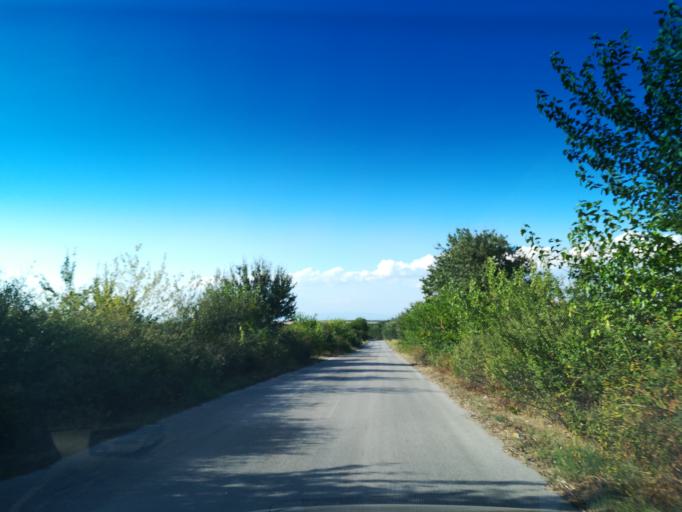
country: BG
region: Khaskovo
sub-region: Obshtina Mineralni Bani
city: Mineralni Bani
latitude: 42.0527
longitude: 25.2708
